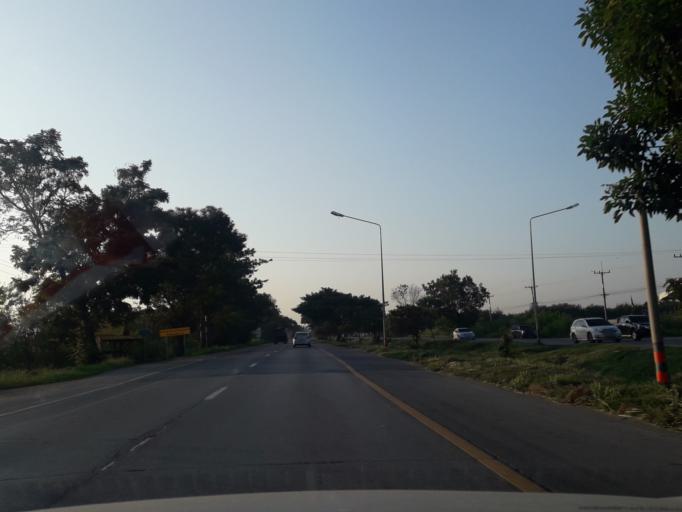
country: TH
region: Phra Nakhon Si Ayutthaya
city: Bang Pa-in
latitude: 14.2650
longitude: 100.5329
